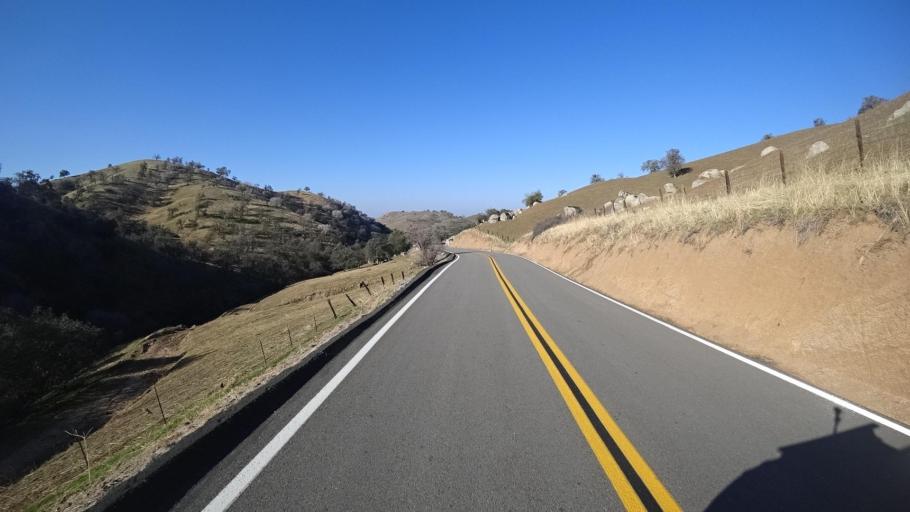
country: US
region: California
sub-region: Kern County
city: Alta Sierra
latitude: 35.7152
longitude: -118.8134
